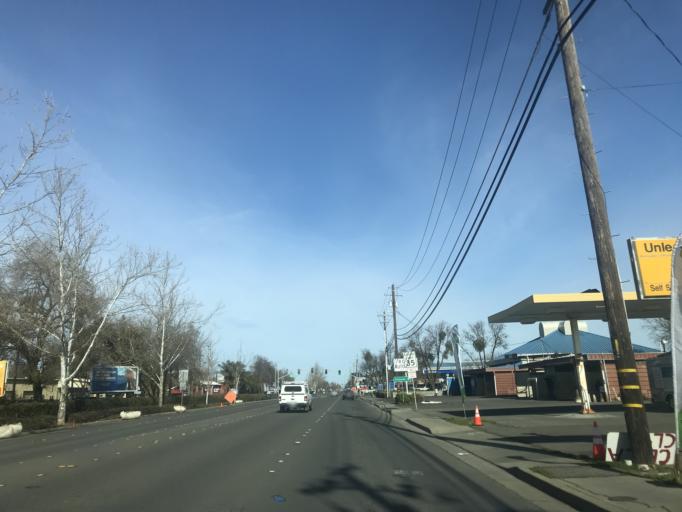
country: US
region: California
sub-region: Yolo County
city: Woodland
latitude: 38.6668
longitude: -121.7655
